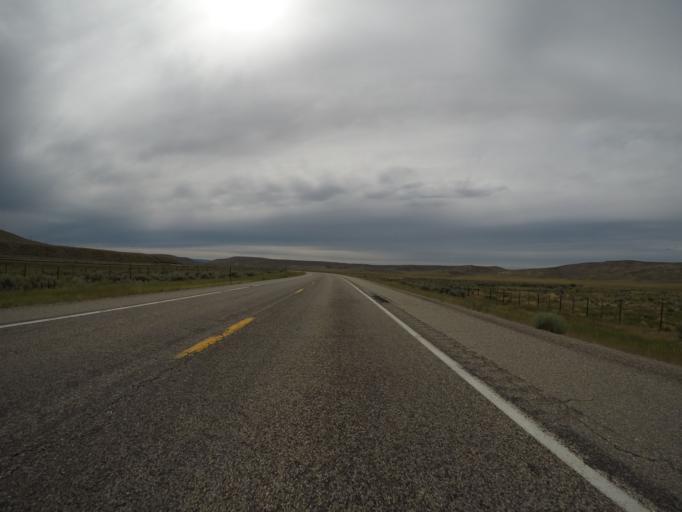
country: US
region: Utah
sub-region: Rich County
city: Randolph
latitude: 41.8255
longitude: -110.9166
